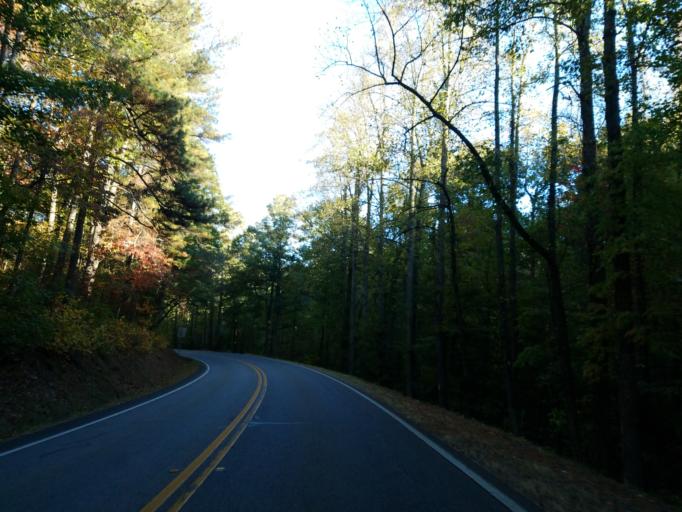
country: US
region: Georgia
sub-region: Pickens County
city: Nelson
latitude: 34.4167
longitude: -84.2646
